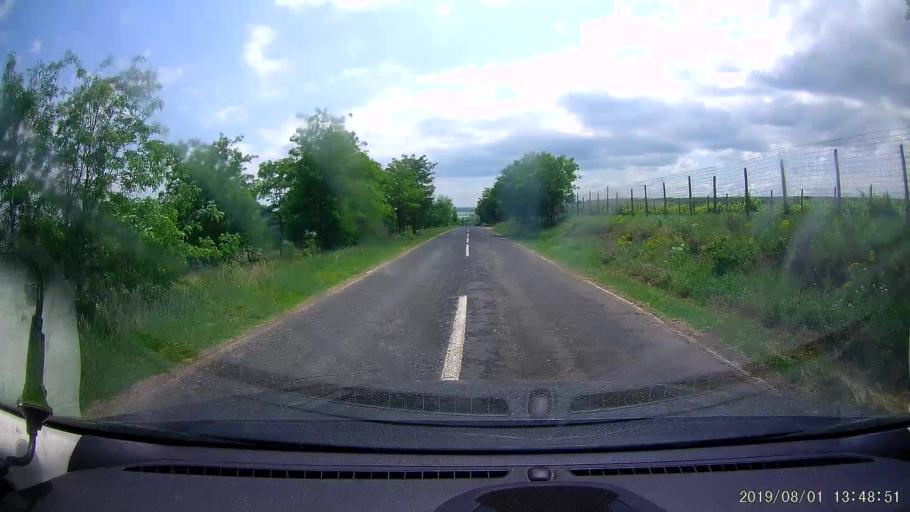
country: RO
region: Galati
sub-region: Comuna Oancea
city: Oancea
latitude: 45.9018
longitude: 28.1094
